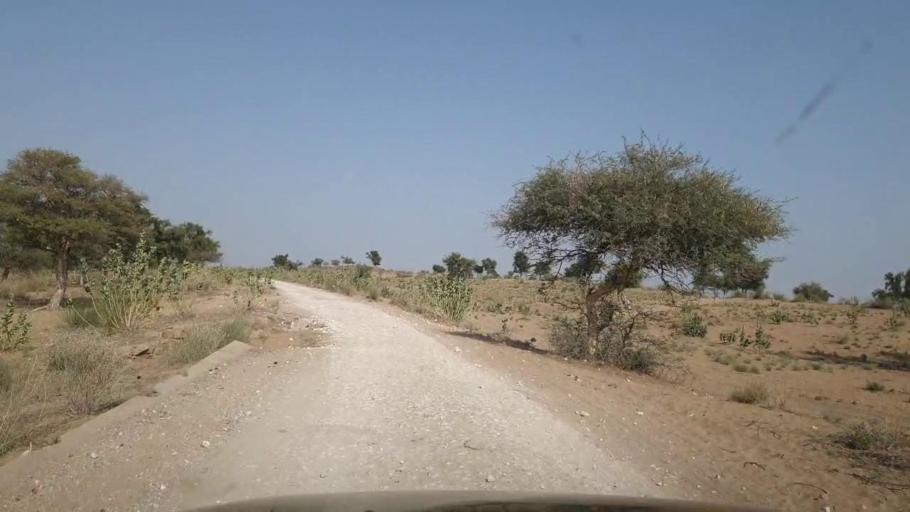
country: PK
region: Sindh
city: Islamkot
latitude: 25.1067
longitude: 70.4205
